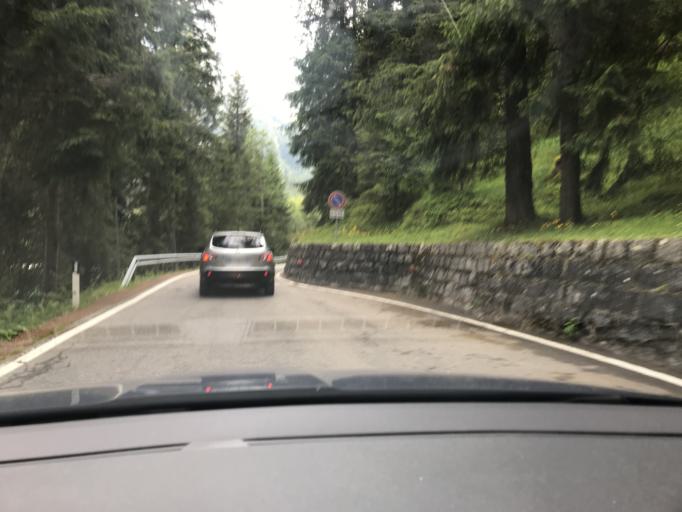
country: IT
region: Trentino-Alto Adige
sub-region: Bolzano
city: San Martino
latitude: 46.8851
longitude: 12.1704
